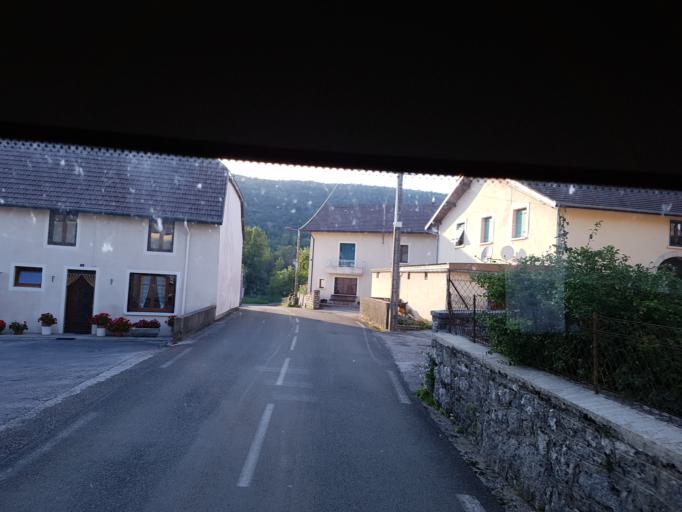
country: FR
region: Franche-Comte
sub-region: Departement du Jura
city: Moirans-en-Montagne
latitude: 46.4030
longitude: 5.6501
